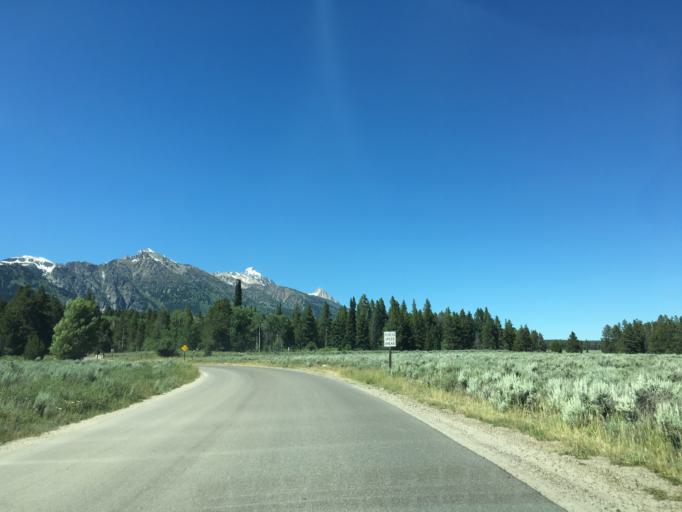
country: US
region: Wyoming
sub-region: Teton County
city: Moose Wilson Road
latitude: 43.6035
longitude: -110.7930
